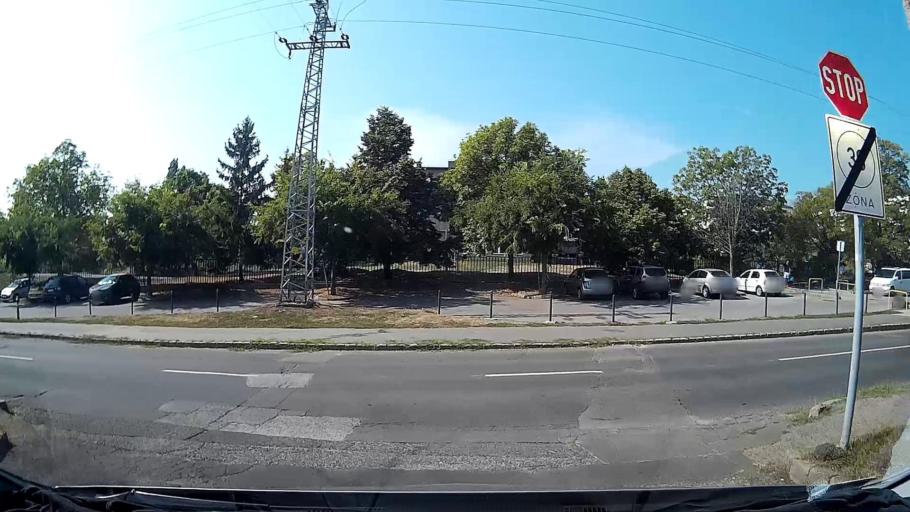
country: HU
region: Pest
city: Szentendre
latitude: 47.6705
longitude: 19.0589
